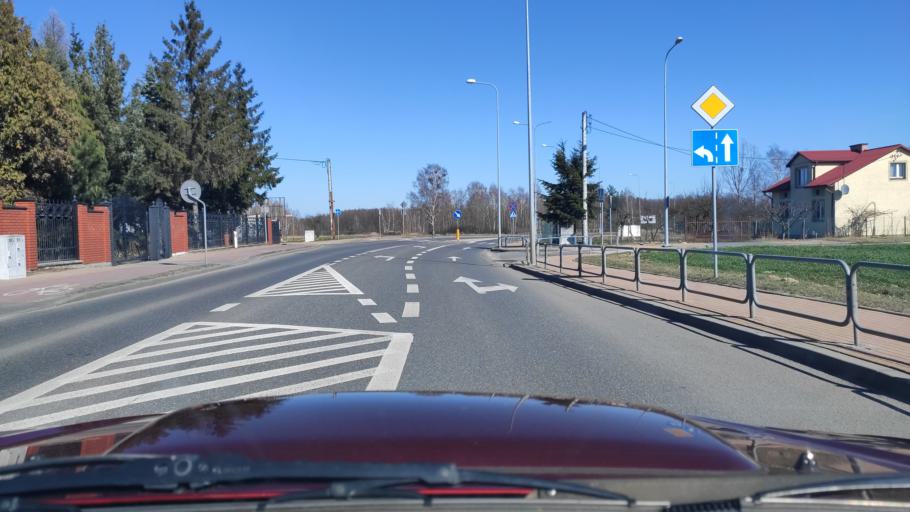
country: PL
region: Masovian Voivodeship
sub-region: Powiat zwolenski
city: Zwolen
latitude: 51.3717
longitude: 21.5870
